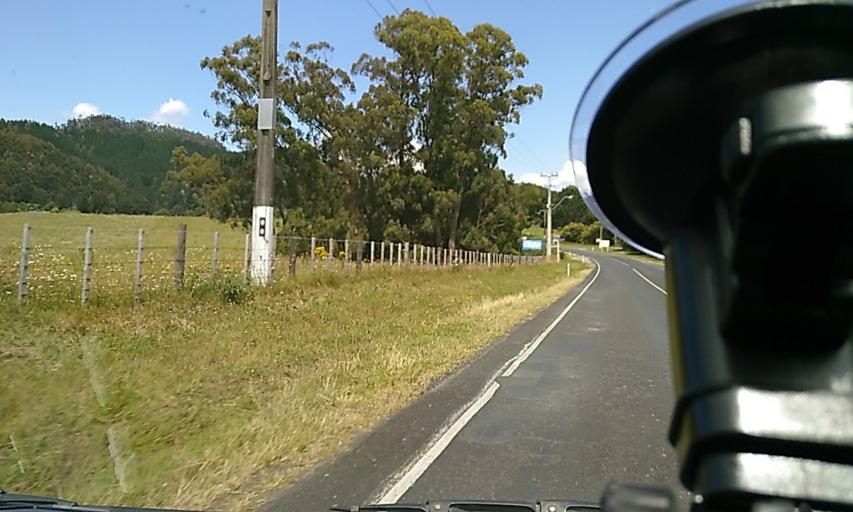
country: NZ
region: Bay of Plenty
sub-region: Western Bay of Plenty District
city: Waihi Beach
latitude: -37.4565
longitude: 175.9350
